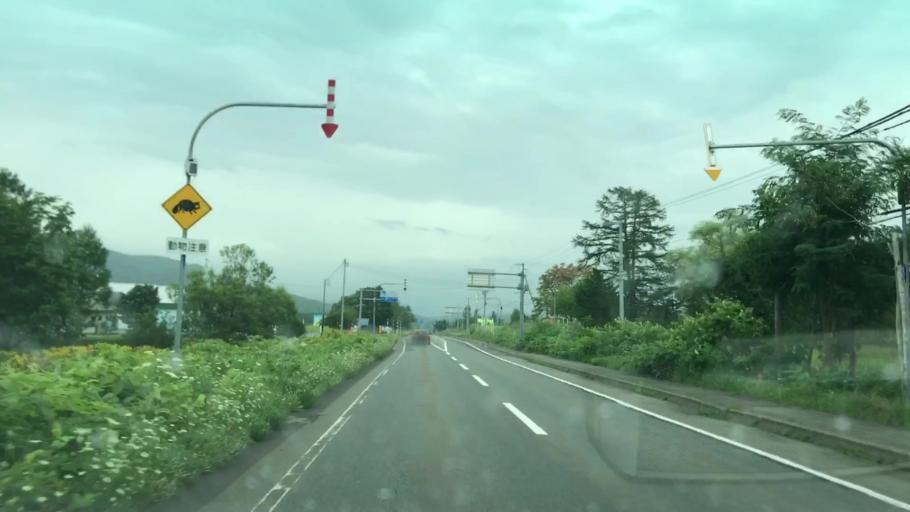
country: JP
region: Hokkaido
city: Niseko Town
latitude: 42.7609
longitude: 140.4787
